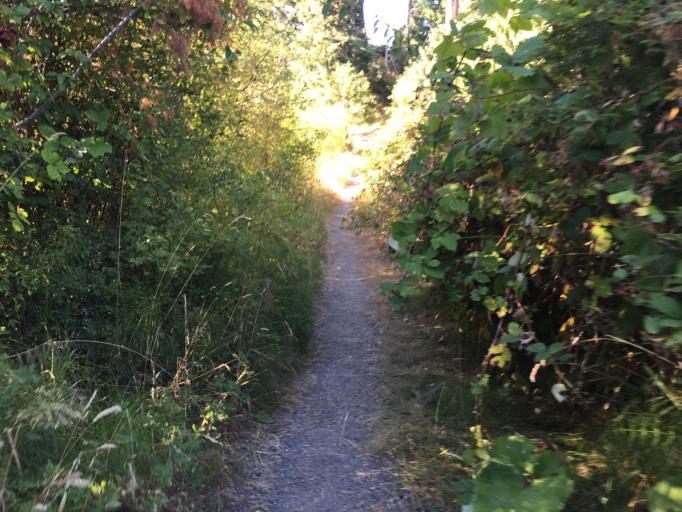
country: CA
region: British Columbia
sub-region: Regional District of Nanaimo
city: Parksville
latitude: 49.3030
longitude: -124.2378
